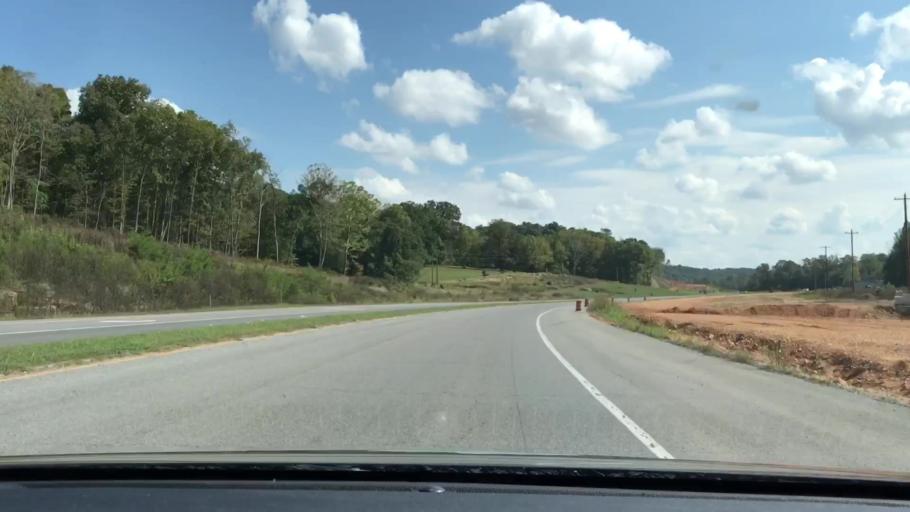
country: US
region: Kentucky
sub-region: Trigg County
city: Cadiz
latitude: 36.8056
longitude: -87.9262
